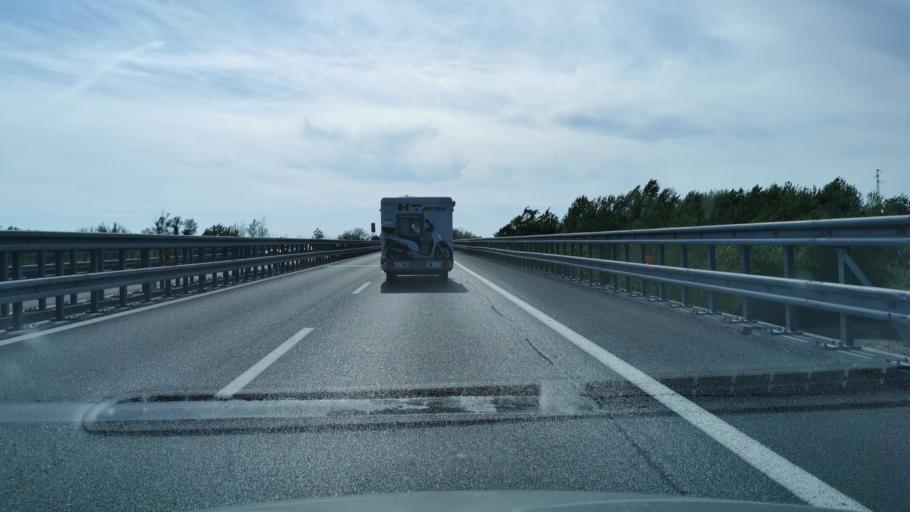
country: IT
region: Piedmont
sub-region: Provincia di Alessandria
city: Tortona
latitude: 44.9177
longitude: 8.8535
